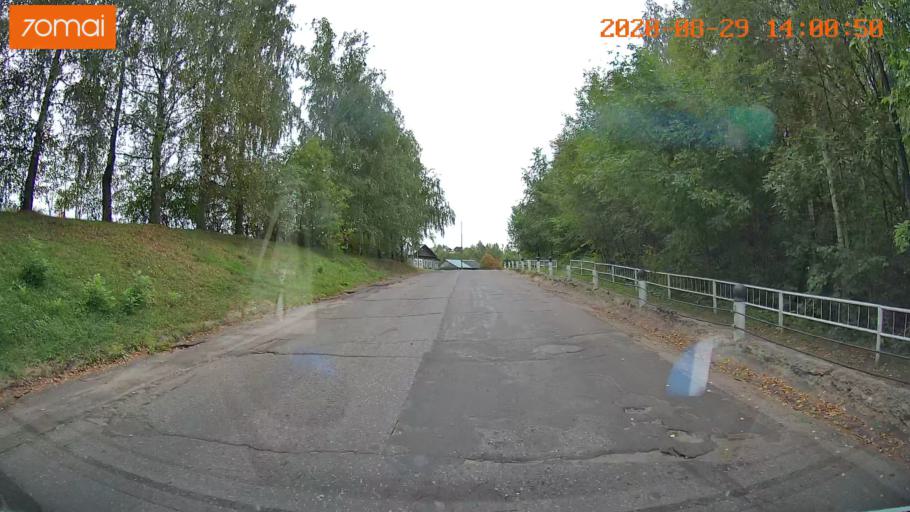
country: RU
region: Ivanovo
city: Yur'yevets
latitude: 57.3138
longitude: 43.1073
